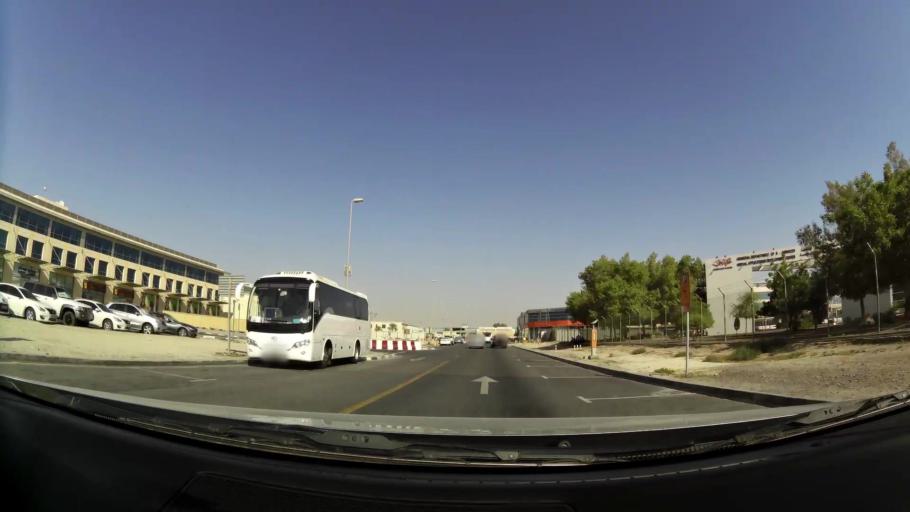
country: AE
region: Dubai
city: Dubai
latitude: 25.1255
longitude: 55.2069
